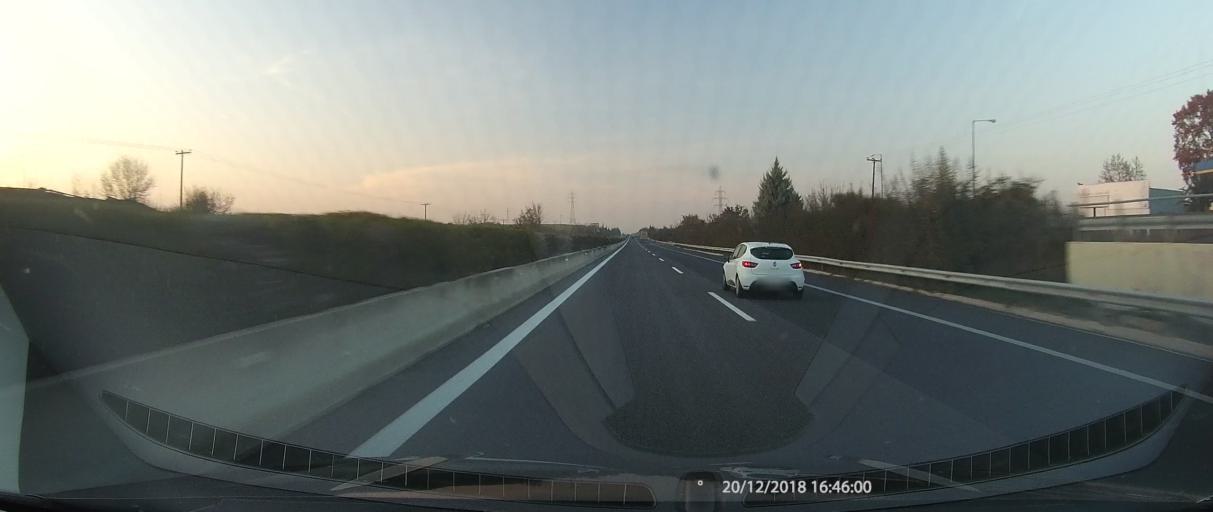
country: GR
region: Thessaly
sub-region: Nomos Magnisias
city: Stefanoviki
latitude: 39.4507
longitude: 22.6802
